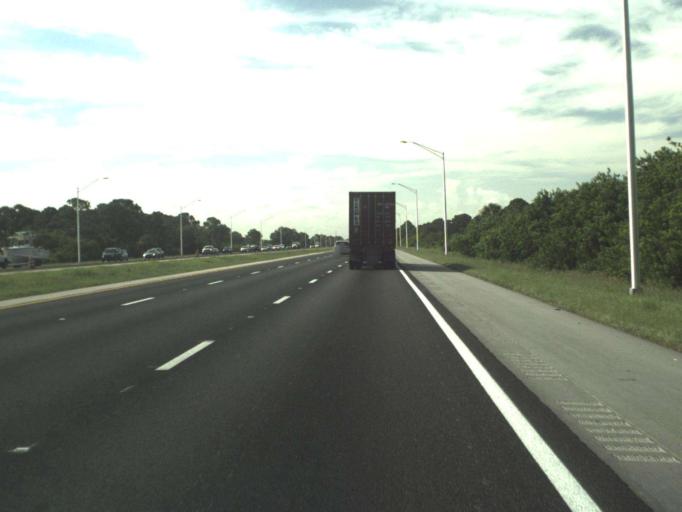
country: US
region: Florida
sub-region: Indian River County
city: West Vero Corridor
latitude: 27.5849
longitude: -80.4988
